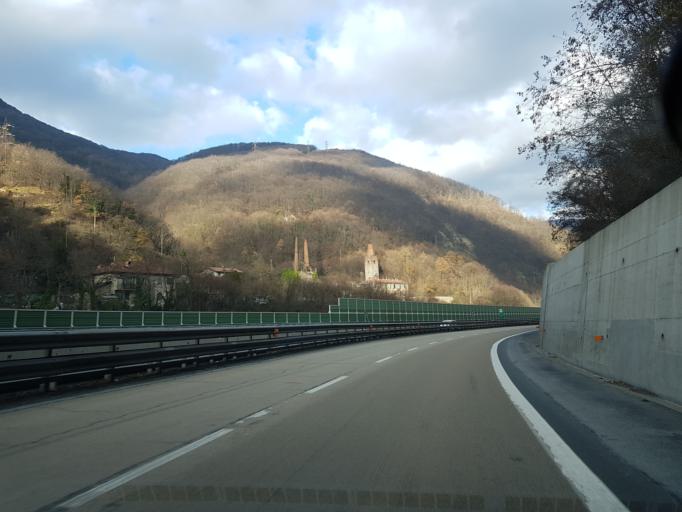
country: IT
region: Liguria
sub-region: Provincia di Genova
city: Ronco Scrivia
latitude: 44.6315
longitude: 8.9432
